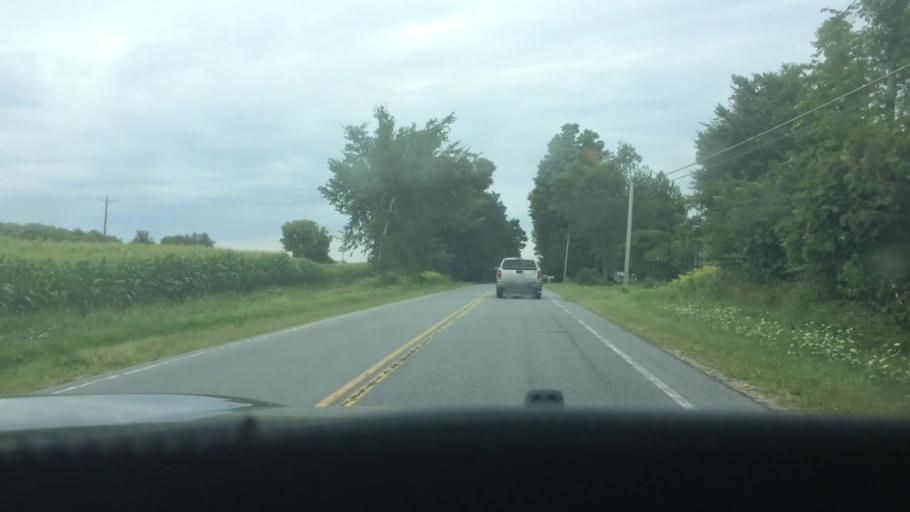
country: US
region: New York
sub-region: St. Lawrence County
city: Canton
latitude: 44.4925
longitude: -75.2165
